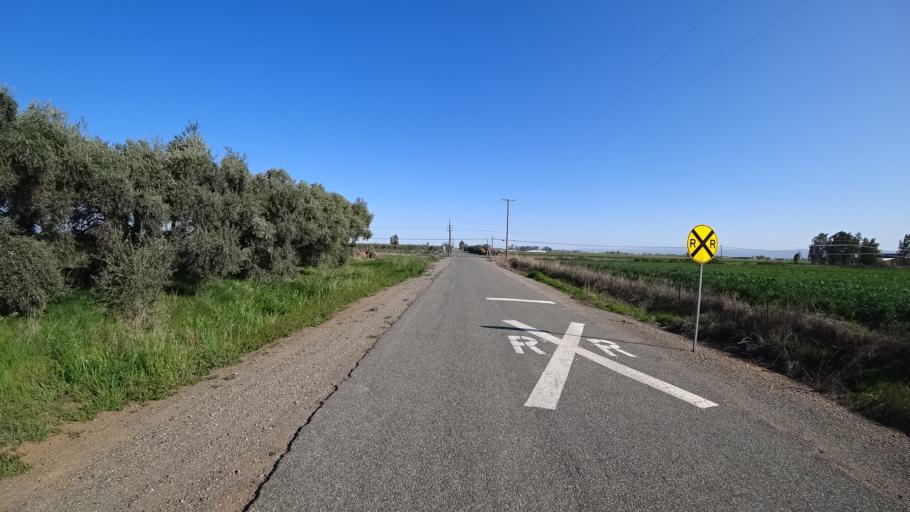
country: US
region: California
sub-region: Glenn County
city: Orland
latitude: 39.7675
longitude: -122.1228
